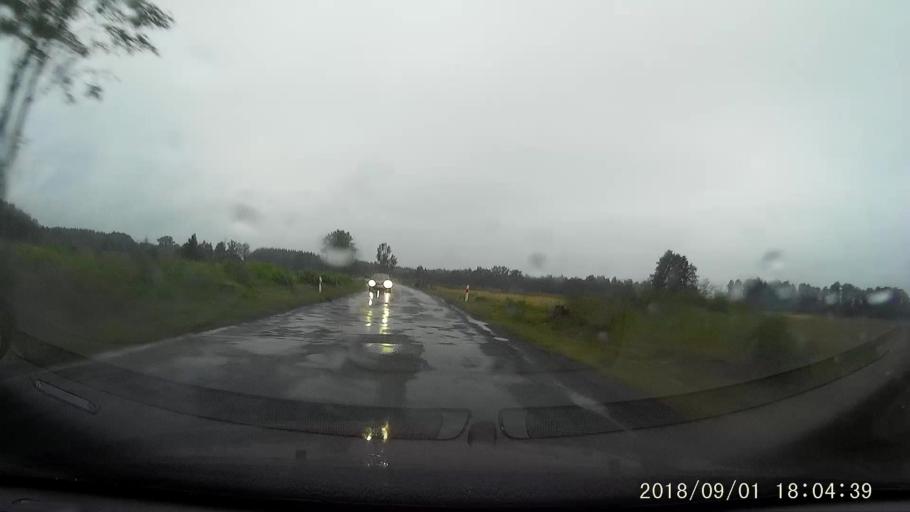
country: PL
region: Lubusz
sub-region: Powiat zaganski
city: Gozdnica
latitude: 51.3690
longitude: 15.1633
